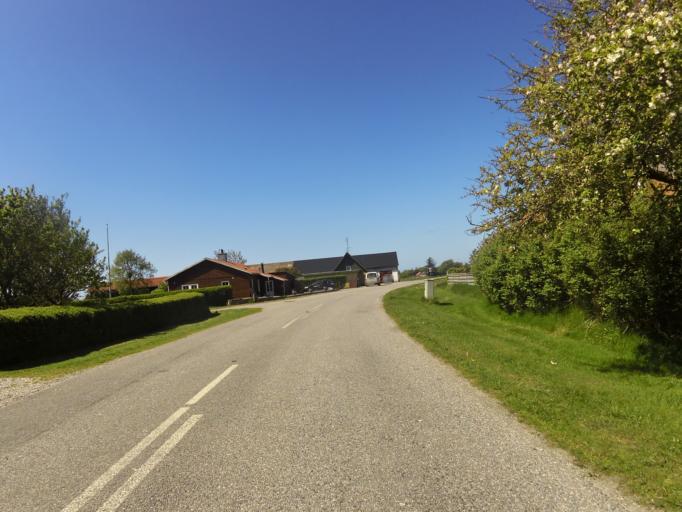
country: DK
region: South Denmark
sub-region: Tonder Kommune
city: Sherrebek
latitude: 55.2239
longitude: 8.7247
